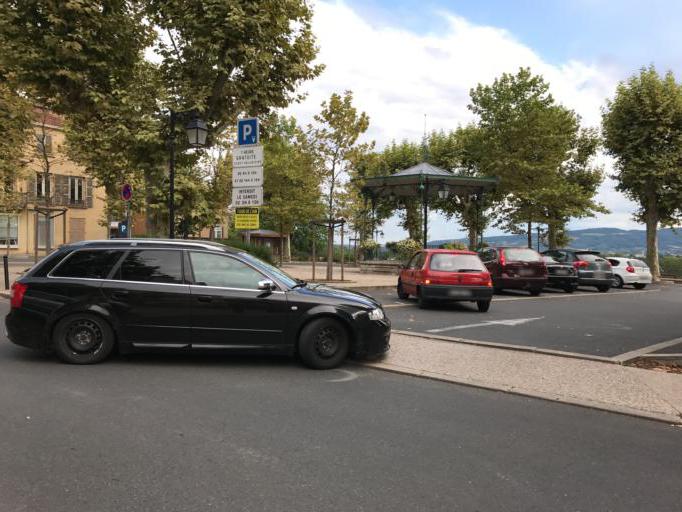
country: FR
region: Rhone-Alpes
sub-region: Departement de l'Ain
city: Trevoux
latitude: 45.9404
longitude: 4.7764
